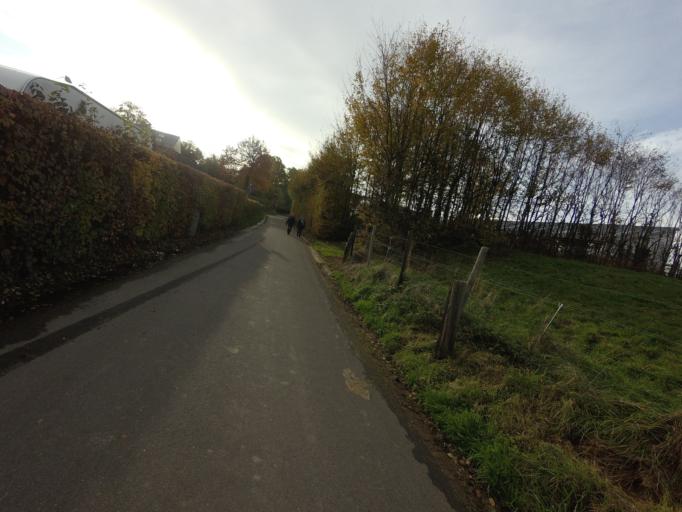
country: NL
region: Limburg
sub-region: Gemeente Simpelveld
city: Simpelveld
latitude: 50.7900
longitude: 5.9556
